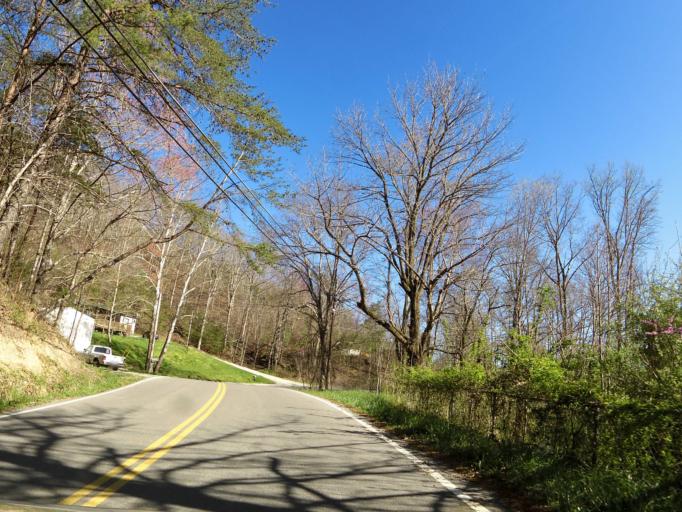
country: US
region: Tennessee
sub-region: Scott County
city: Huntsville
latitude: 36.3583
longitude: -84.3970
